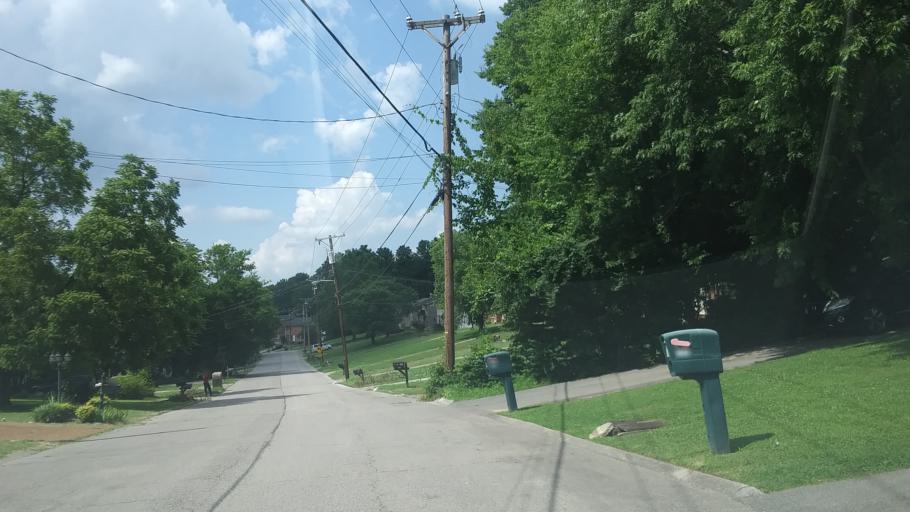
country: US
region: Tennessee
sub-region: Davidson County
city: Oak Hill
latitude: 36.0709
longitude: -86.7103
